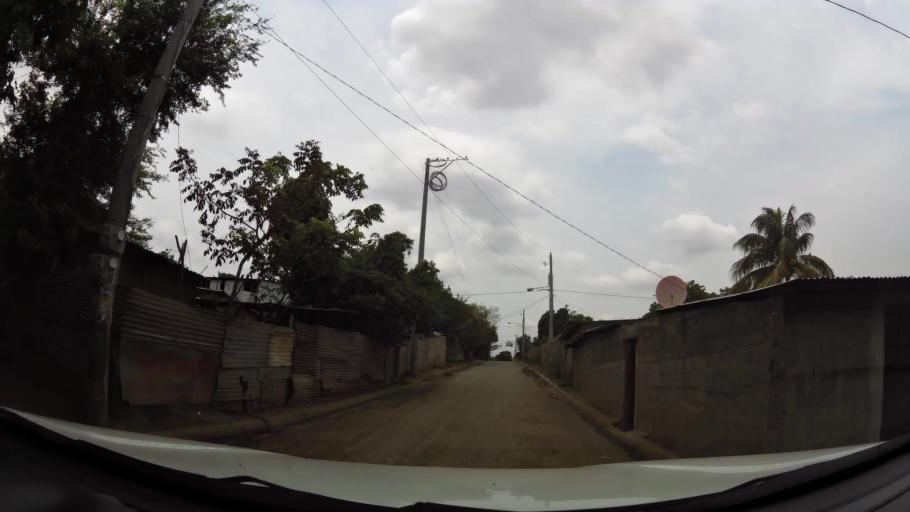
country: NI
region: Managua
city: Managua
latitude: 12.1100
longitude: -86.2196
